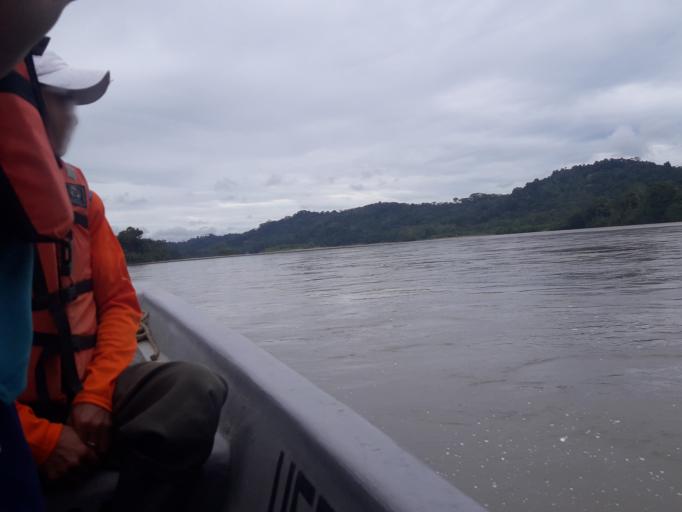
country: EC
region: Orellana
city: Boca Suno
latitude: -0.8788
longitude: -77.2868
